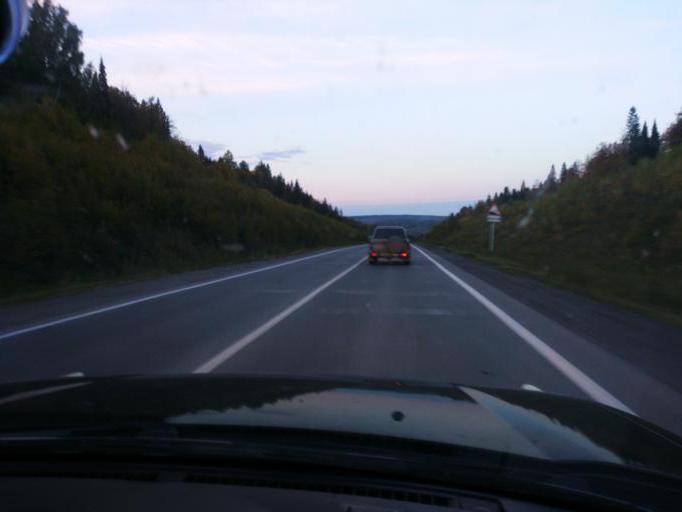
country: RU
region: Perm
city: Sylva
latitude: 58.2915
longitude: 56.7498
